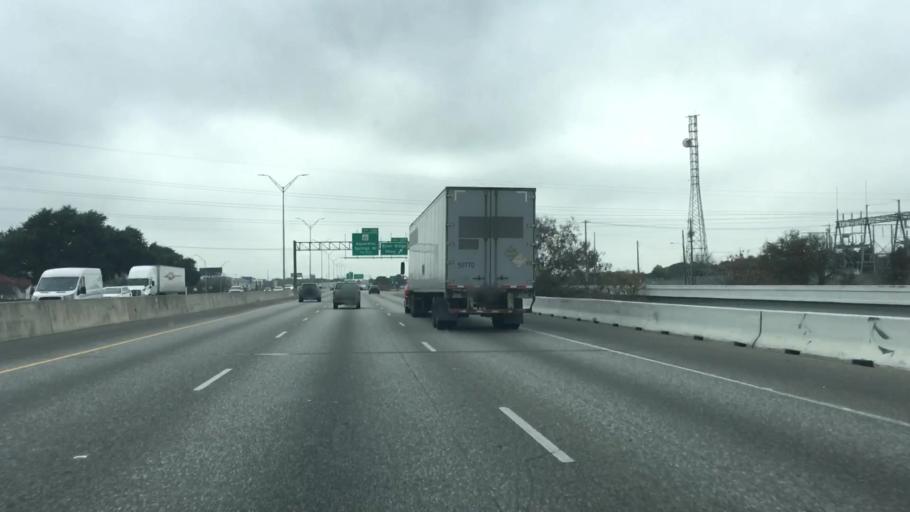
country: US
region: Texas
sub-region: Hays County
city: San Marcos
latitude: 29.9125
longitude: -97.8983
